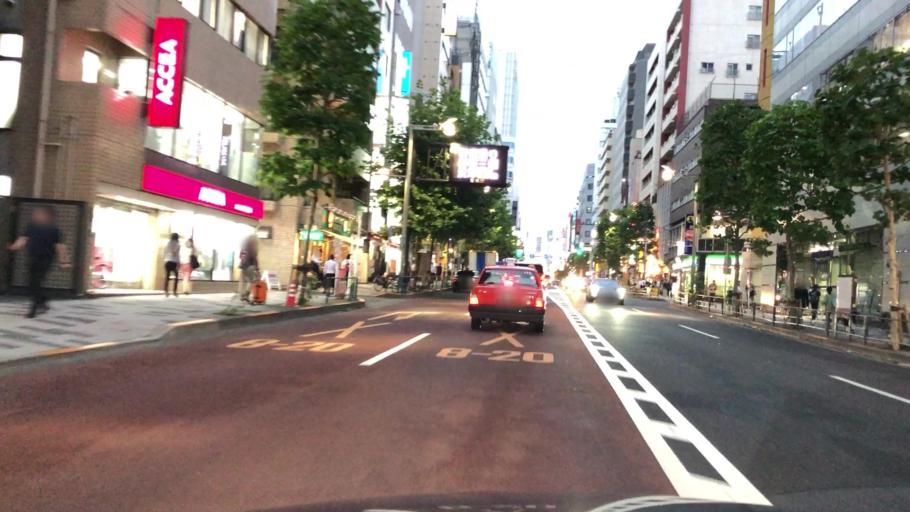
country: JP
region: Tokyo
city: Tokyo
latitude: 35.6890
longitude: 139.7089
